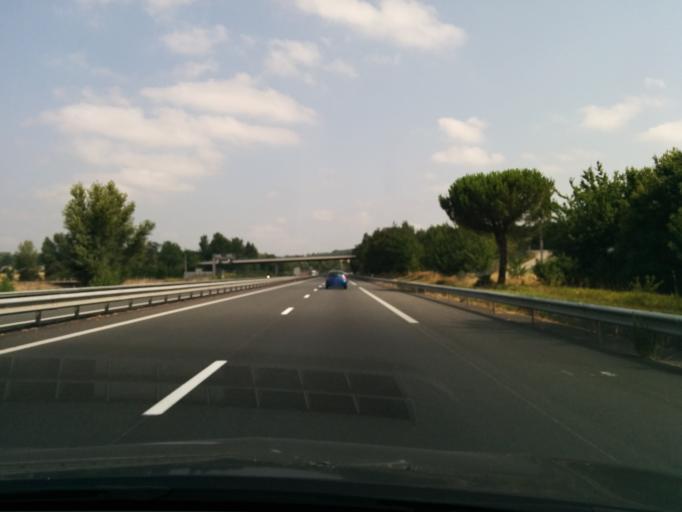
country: FR
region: Midi-Pyrenees
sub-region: Departement de la Haute-Garonne
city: Garidech
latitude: 43.6982
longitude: 1.5683
